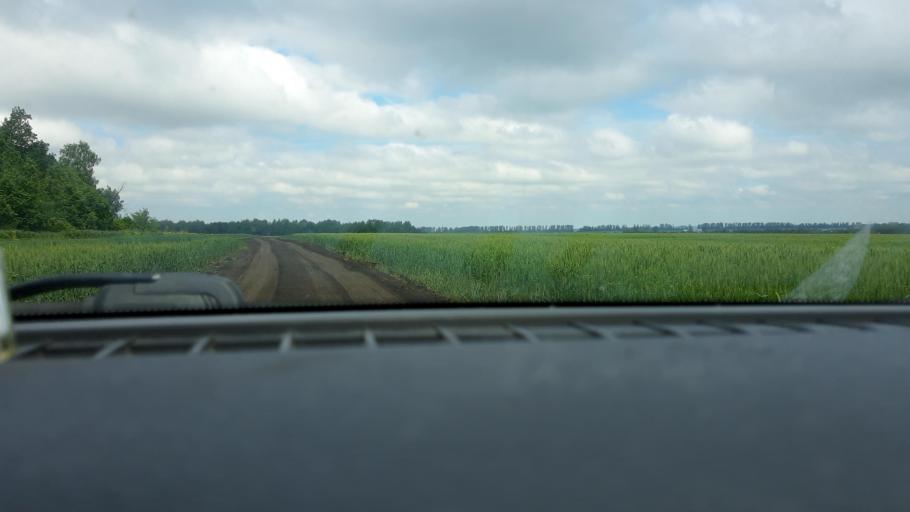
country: RU
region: Bashkortostan
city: Dmitriyevka
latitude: 54.7069
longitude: 55.4965
